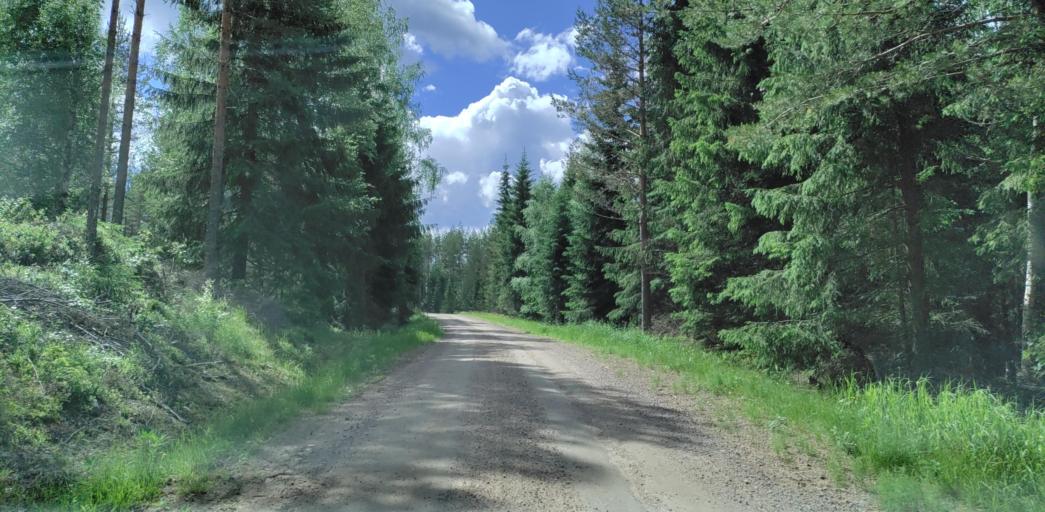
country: SE
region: Vaermland
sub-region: Hagfors Kommun
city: Ekshaerad
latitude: 60.1012
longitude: 13.3522
